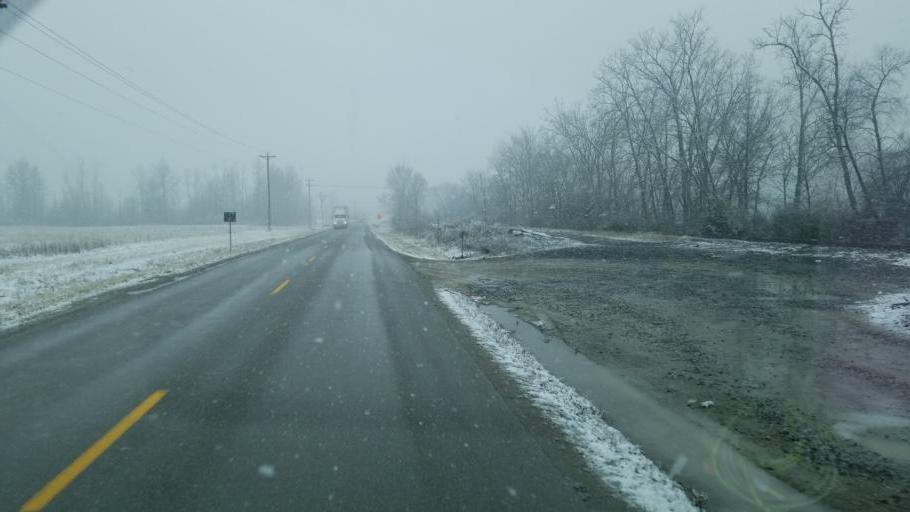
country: US
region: Ohio
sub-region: Champaign County
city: North Lewisburg
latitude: 40.2733
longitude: -83.4926
